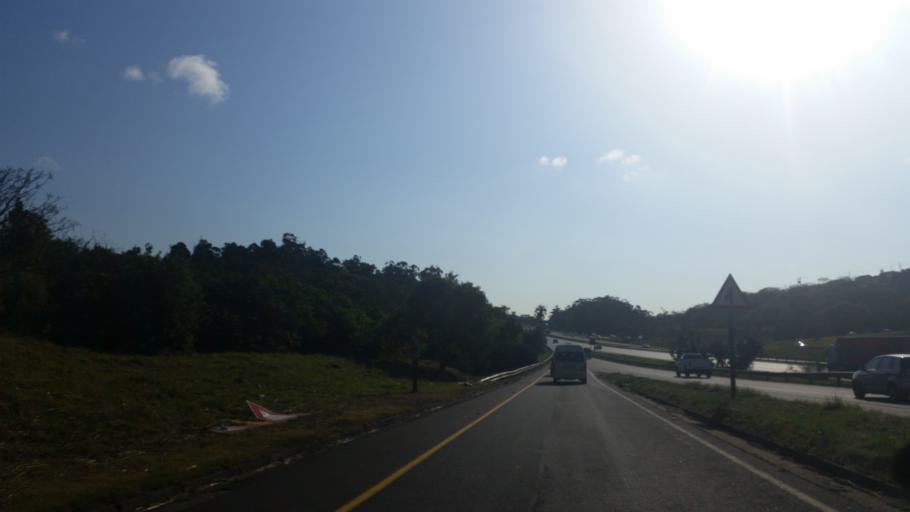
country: ZA
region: KwaZulu-Natal
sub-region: eThekwini Metropolitan Municipality
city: Berea
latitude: -29.8385
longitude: 30.9575
